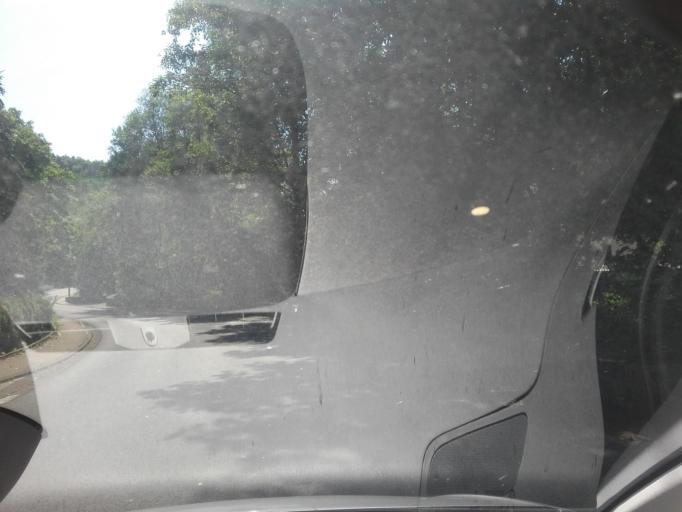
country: DE
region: Saarland
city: Mettlach
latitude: 49.4860
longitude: 6.5666
